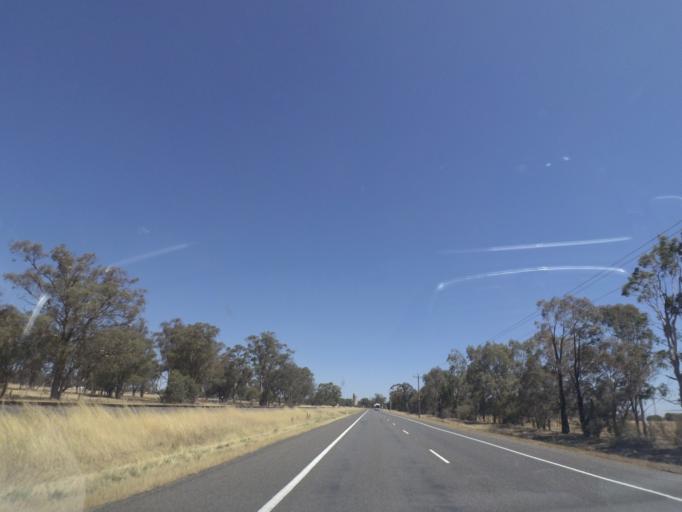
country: AU
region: Victoria
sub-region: Greater Shepparton
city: Shepparton
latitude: -36.2303
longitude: 145.4318
